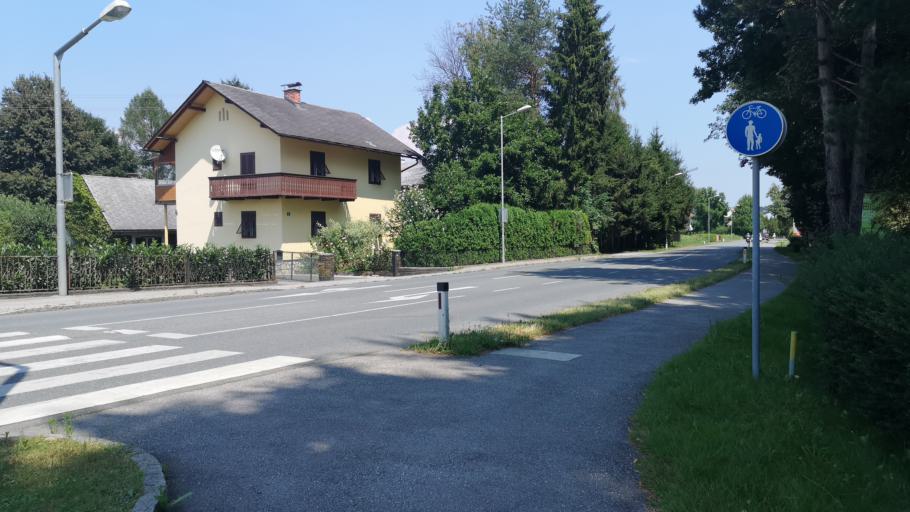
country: AT
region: Styria
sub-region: Politischer Bezirk Deutschlandsberg
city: Deutschlandsberg
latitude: 46.8216
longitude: 15.2554
